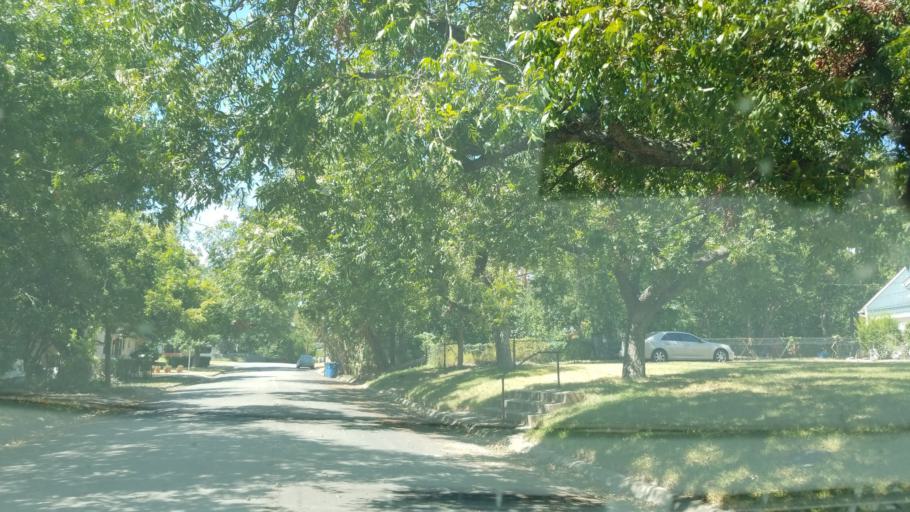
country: US
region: Texas
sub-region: Dallas County
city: Dallas
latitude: 32.7641
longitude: -96.8303
